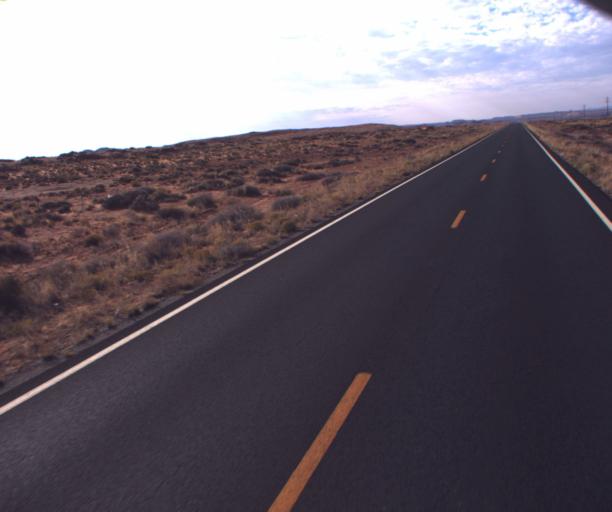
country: US
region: Arizona
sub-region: Apache County
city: Many Farms
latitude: 36.8307
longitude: -109.6437
